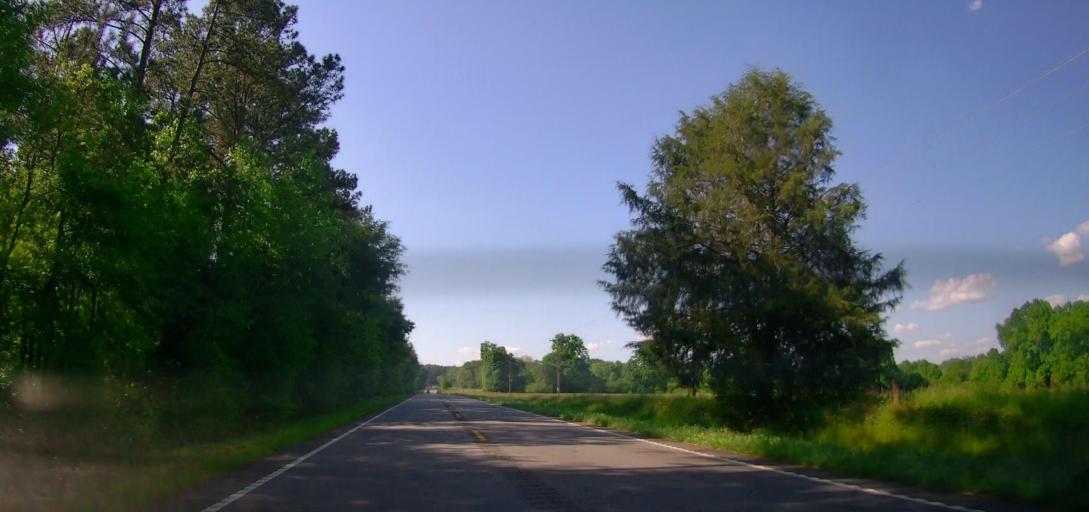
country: US
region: Georgia
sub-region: Morgan County
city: Madison
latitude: 33.6404
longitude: -83.4922
